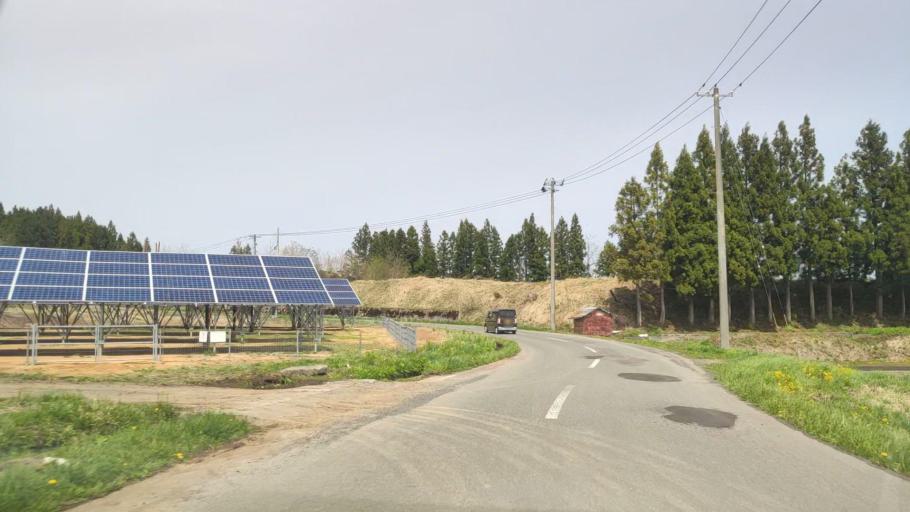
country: JP
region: Aomori
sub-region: Misawa Shi
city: Inuotose
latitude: 40.7718
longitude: 141.1227
